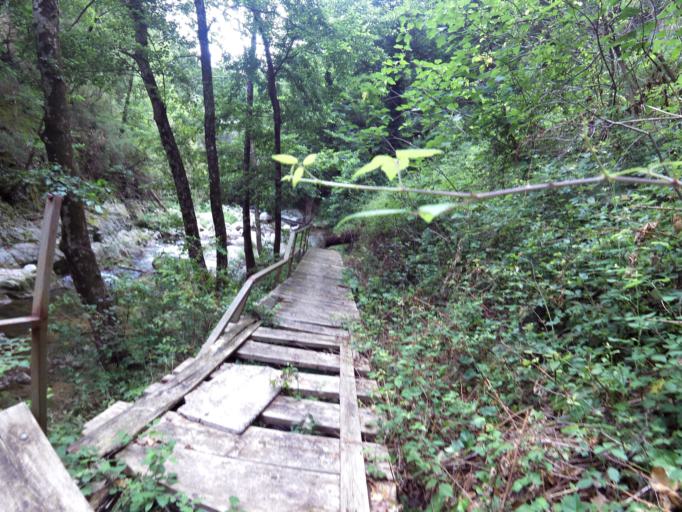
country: IT
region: Calabria
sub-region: Provincia di Reggio Calabria
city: Bivongi
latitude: 38.4886
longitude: 16.4271
